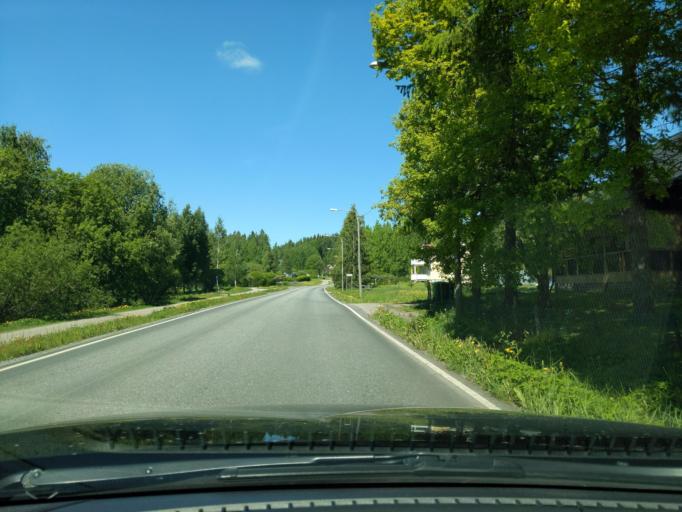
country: FI
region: Paijanne Tavastia
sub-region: Lahti
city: Lahti
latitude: 61.0661
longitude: 25.6631
